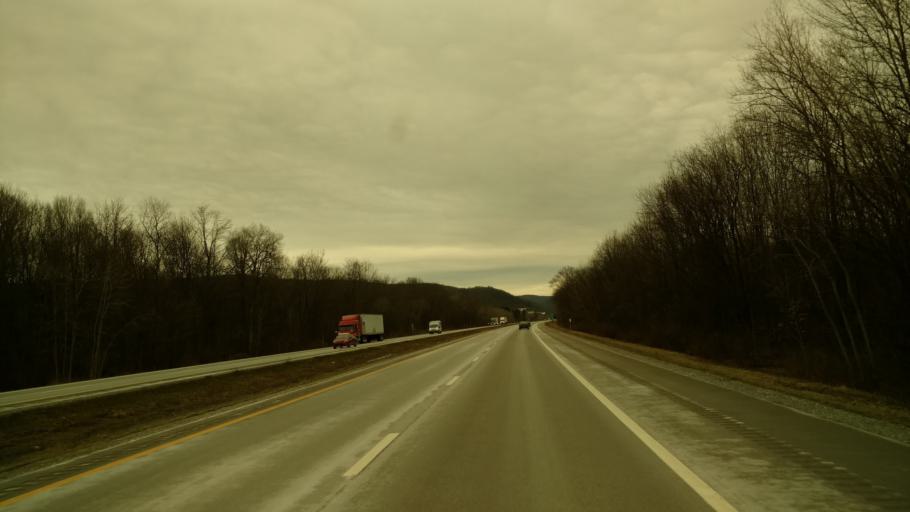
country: US
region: New York
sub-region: Cattaraugus County
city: Allegany
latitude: 42.0868
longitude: -78.5847
